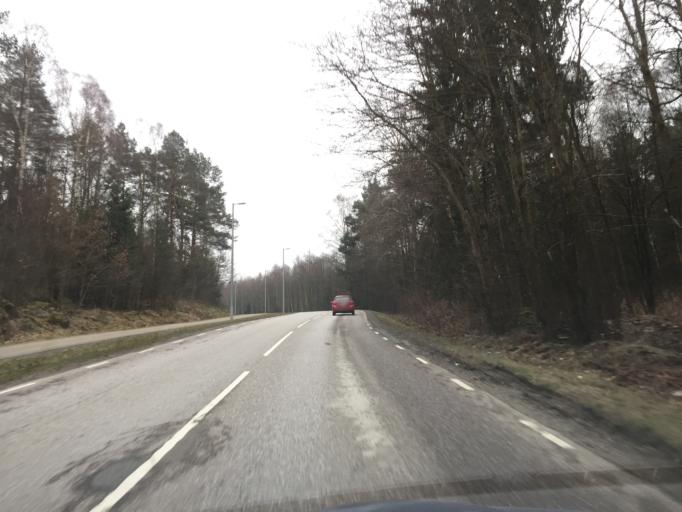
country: SE
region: Vaestra Goetaland
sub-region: Goteborg
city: Rannebergen
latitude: 57.7713
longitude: 12.0736
